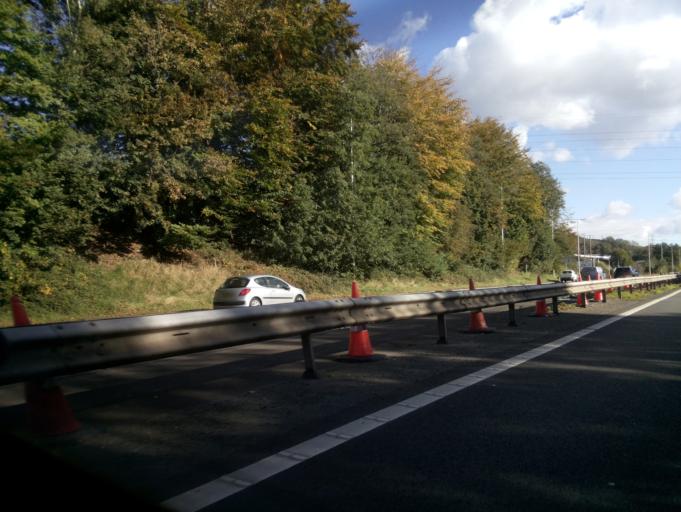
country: GB
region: Wales
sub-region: Caerphilly County Borough
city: Abertridwr
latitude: 51.5781
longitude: -3.2942
